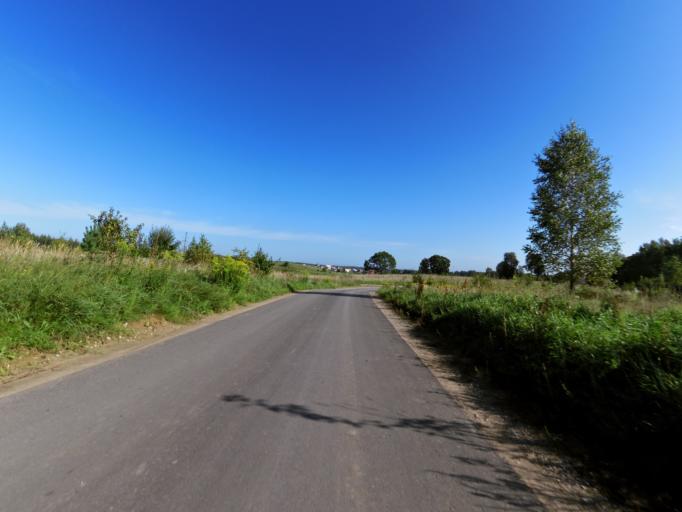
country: LT
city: Grigiskes
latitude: 54.7028
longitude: 25.1195
